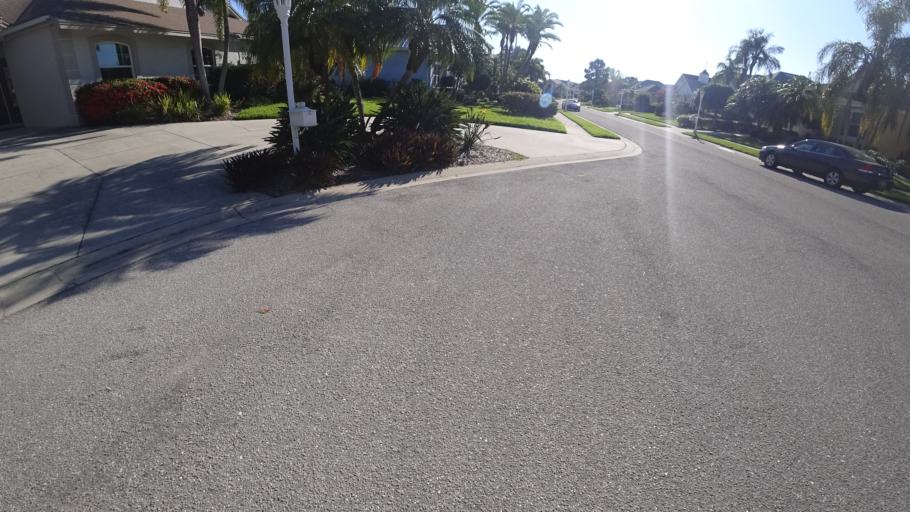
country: US
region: Florida
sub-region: Manatee County
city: Ellenton
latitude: 27.5025
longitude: -82.5038
